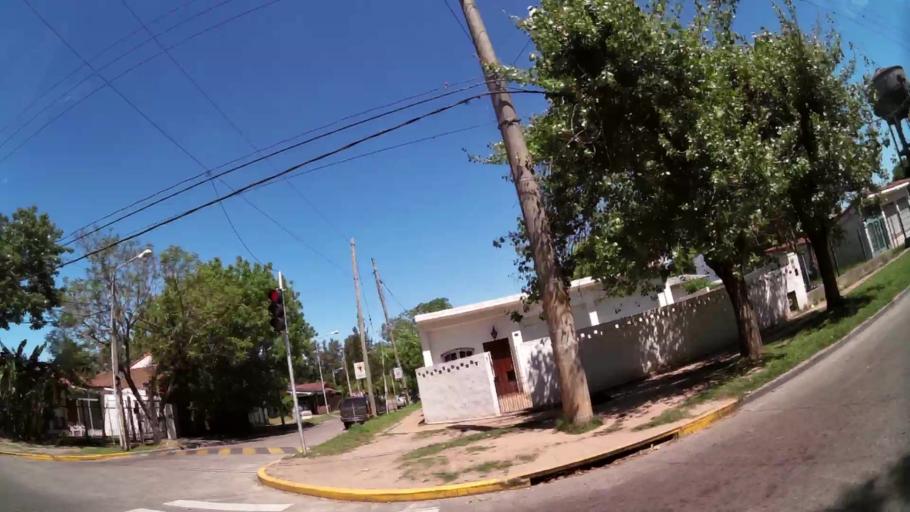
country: AR
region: Buenos Aires
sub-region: Partido de Tigre
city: Tigre
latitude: -34.4911
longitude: -58.6526
